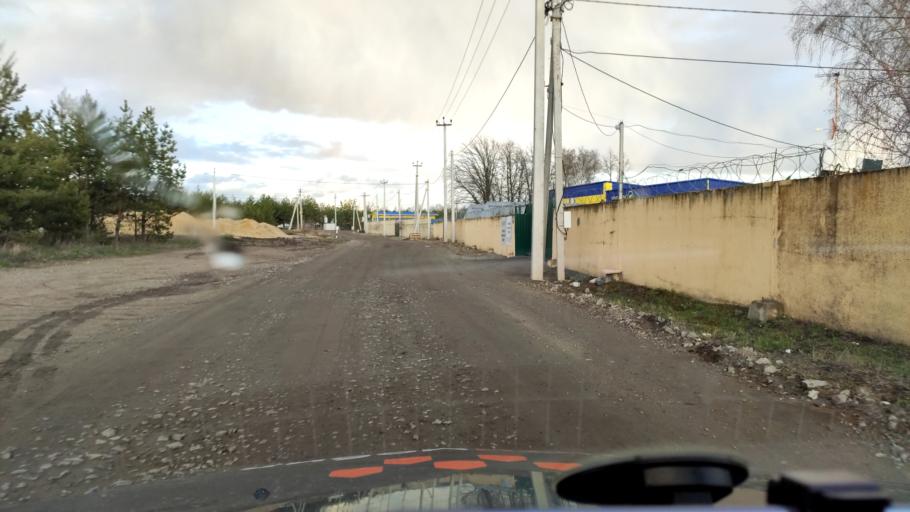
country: RU
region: Voronezj
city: Podgornoye
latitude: 51.8309
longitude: 39.2031
